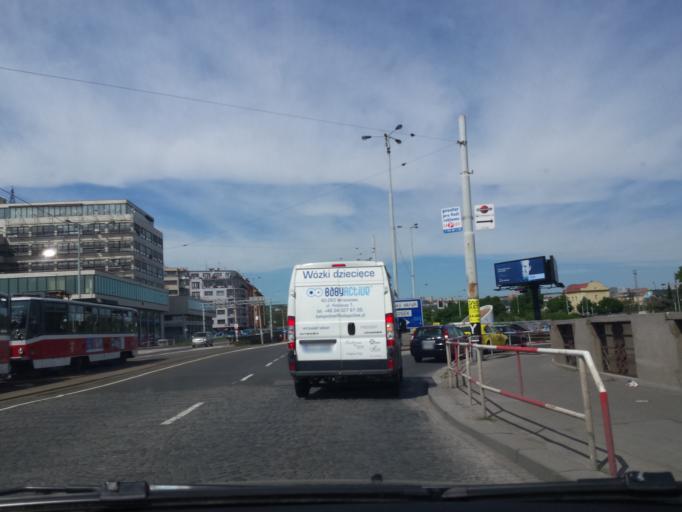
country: CZ
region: Praha
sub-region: Praha 8
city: Karlin
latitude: 50.0974
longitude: 14.4372
